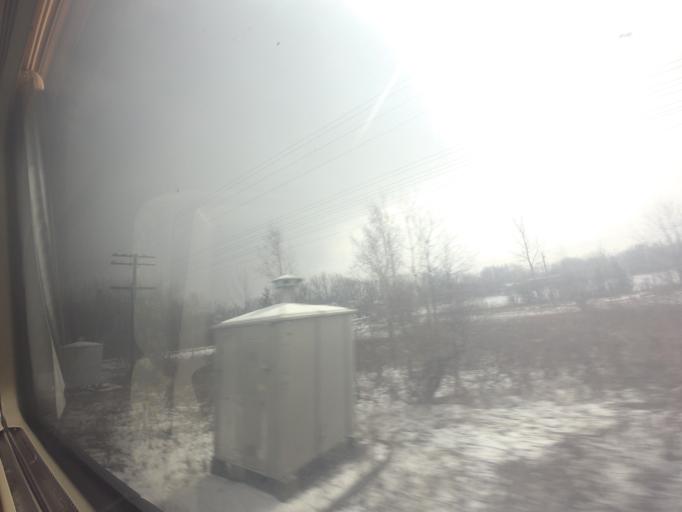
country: CA
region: Ontario
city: Cobourg
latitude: 43.9220
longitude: -78.4424
